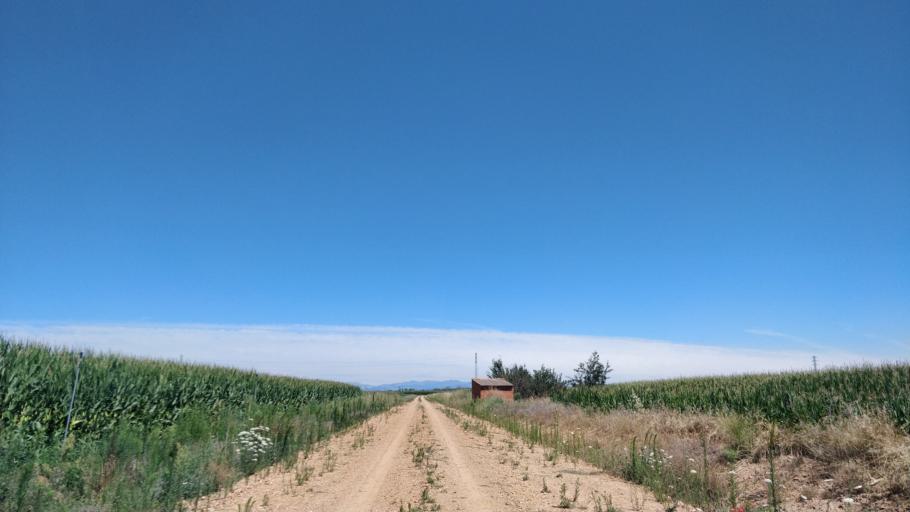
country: ES
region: Castille and Leon
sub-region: Provincia de Leon
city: Bustillo del Paramo
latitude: 42.4568
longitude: -5.8166
